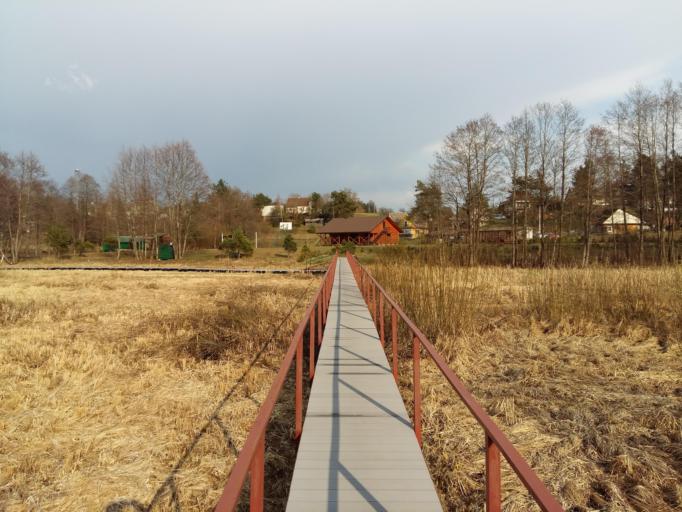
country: LT
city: Svencioneliai
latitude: 55.1567
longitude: 25.9861
